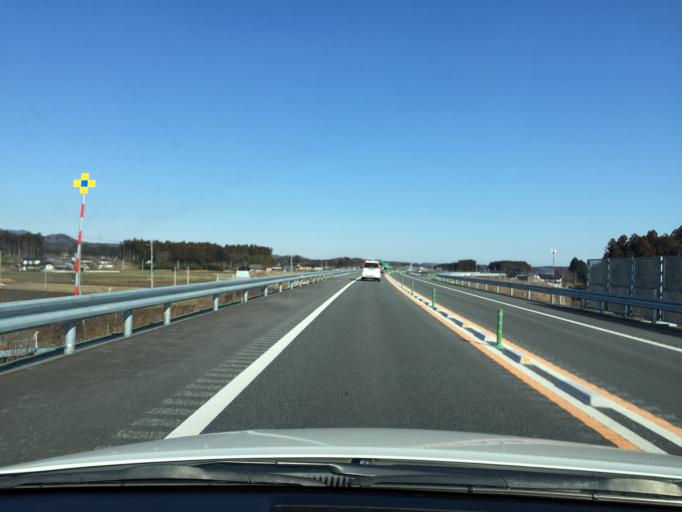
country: JP
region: Fukushima
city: Namie
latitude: 37.6055
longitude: 140.9254
